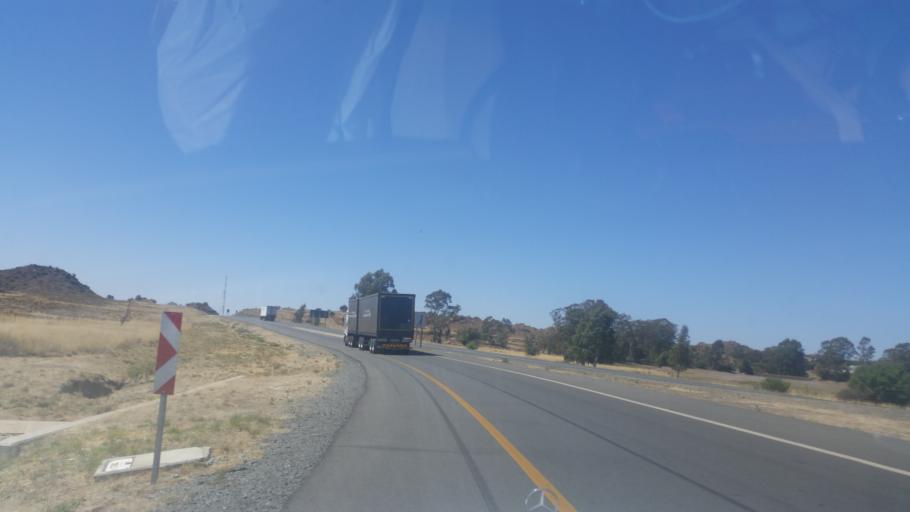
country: ZA
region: Northern Cape
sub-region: Pixley ka Seme District Municipality
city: Colesberg
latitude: -30.7242
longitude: 25.0874
